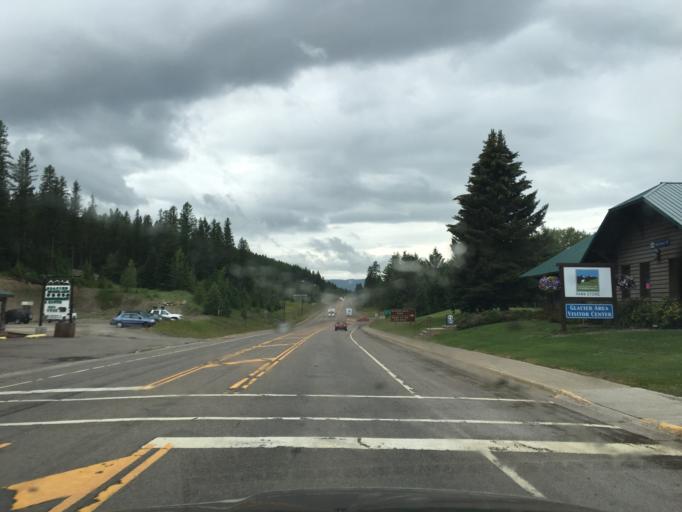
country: US
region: Montana
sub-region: Flathead County
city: Columbia Falls
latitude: 48.4961
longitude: -113.9789
